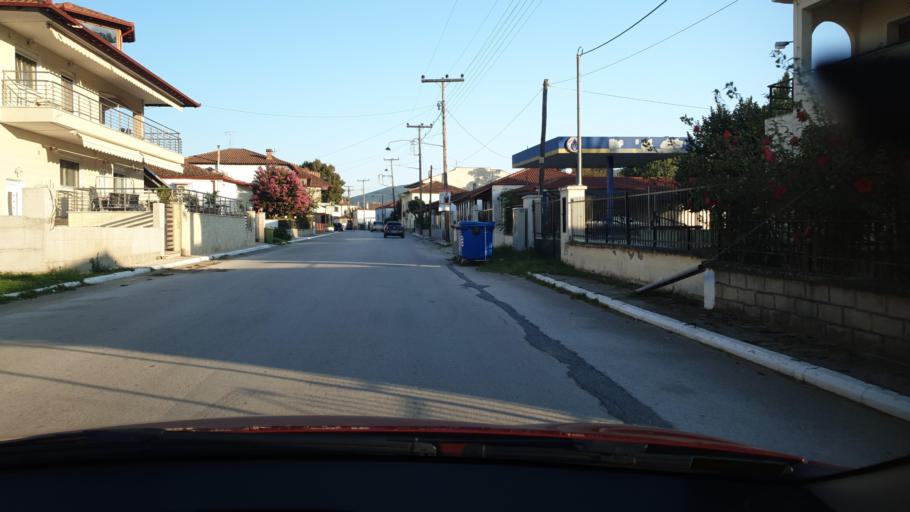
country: GR
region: Central Macedonia
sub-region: Nomos Thessalonikis
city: Gerakarou
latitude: 40.5740
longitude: 23.2854
